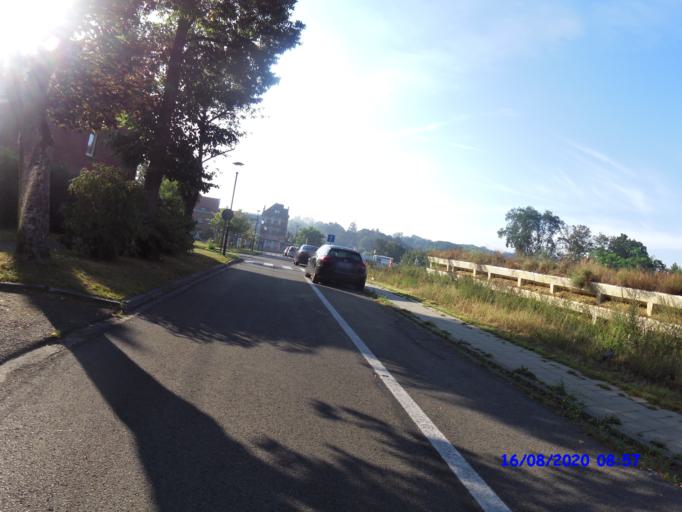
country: BE
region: Flanders
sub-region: Provincie Vlaams-Brabant
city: Linkebeek
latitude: 50.7749
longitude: 4.3381
